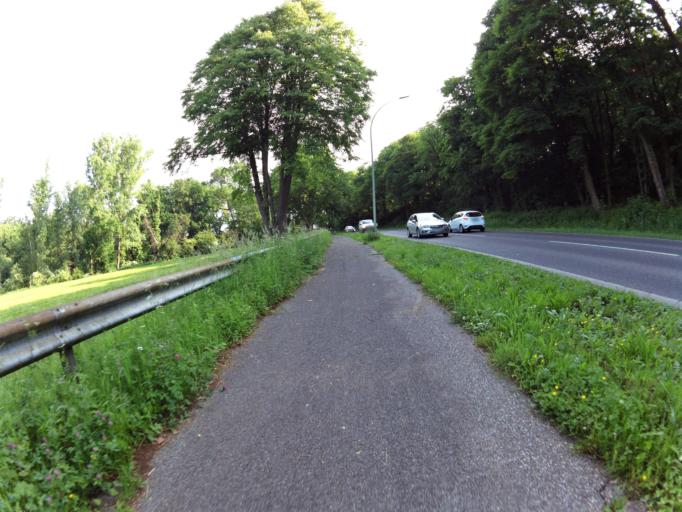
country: DE
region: North Rhine-Westphalia
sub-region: Regierungsbezirk Koln
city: Ubach-Palenberg
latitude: 50.9390
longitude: 6.1050
